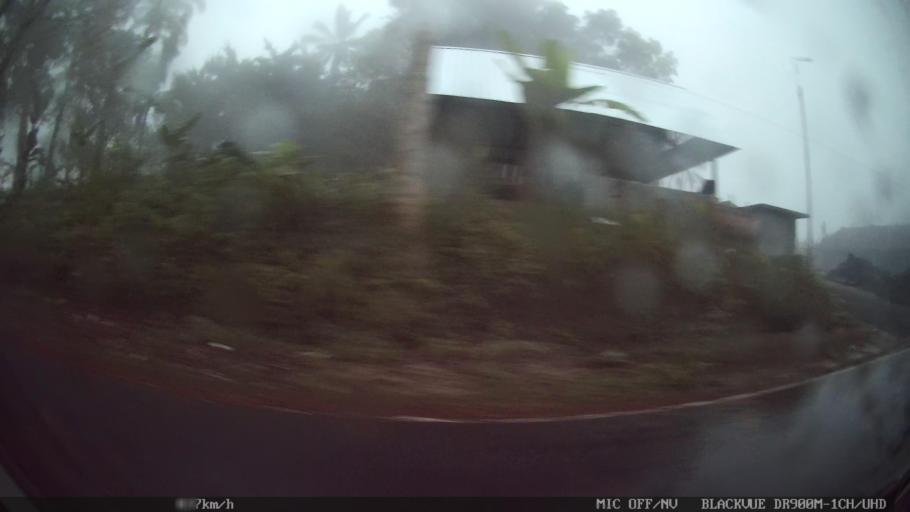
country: ID
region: Bali
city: Banjar Taro Kelod
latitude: -8.3375
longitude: 115.2833
